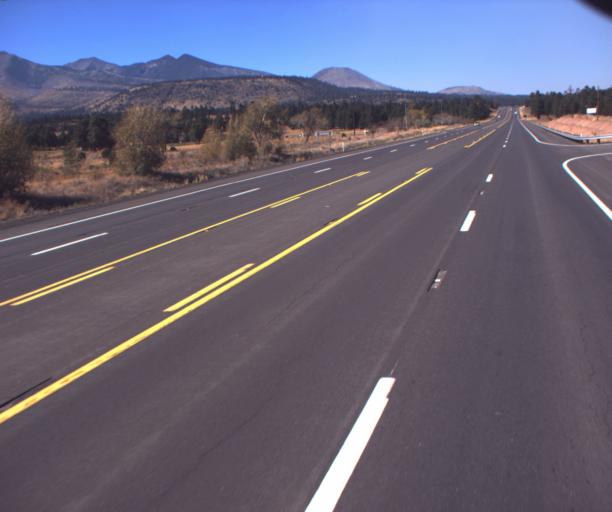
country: US
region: Arizona
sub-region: Coconino County
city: Flagstaff
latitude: 35.3347
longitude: -111.5500
